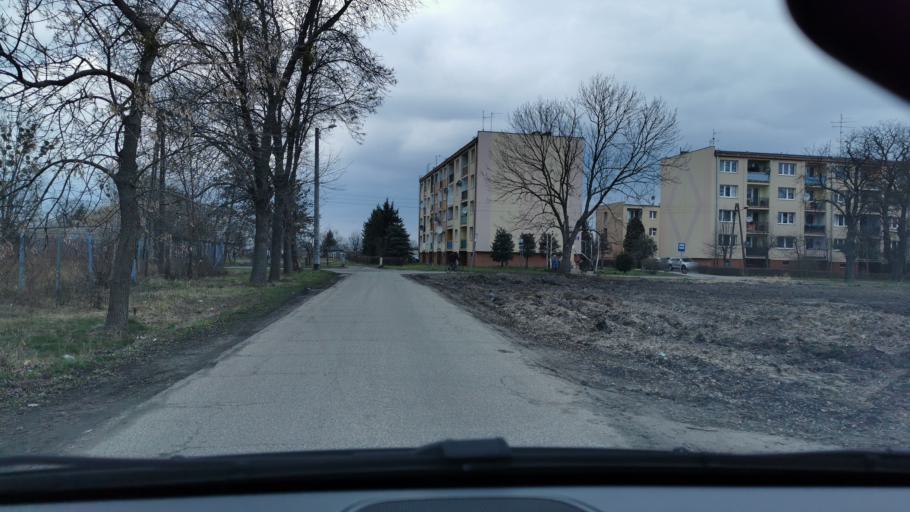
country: PL
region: Masovian Voivodeship
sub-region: Powiat zyrardowski
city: Guzow
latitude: 52.1150
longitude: 20.3269
